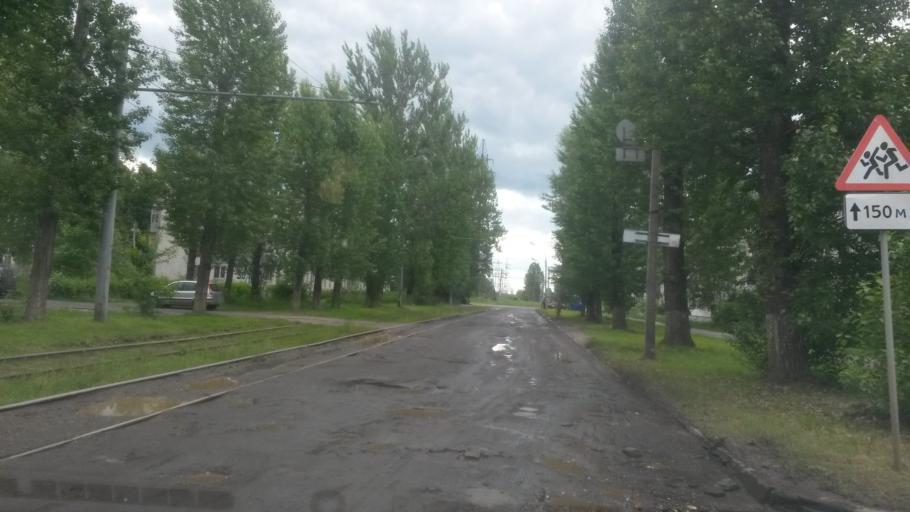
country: RU
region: Jaroslavl
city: Yaroslavl
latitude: 57.6845
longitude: 39.8085
